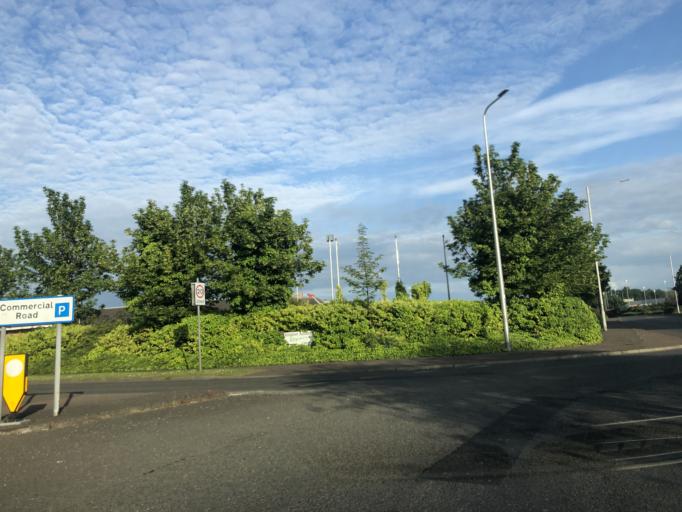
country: GB
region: Scotland
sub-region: Fife
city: Leven
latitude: 56.1961
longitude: -3.0045
